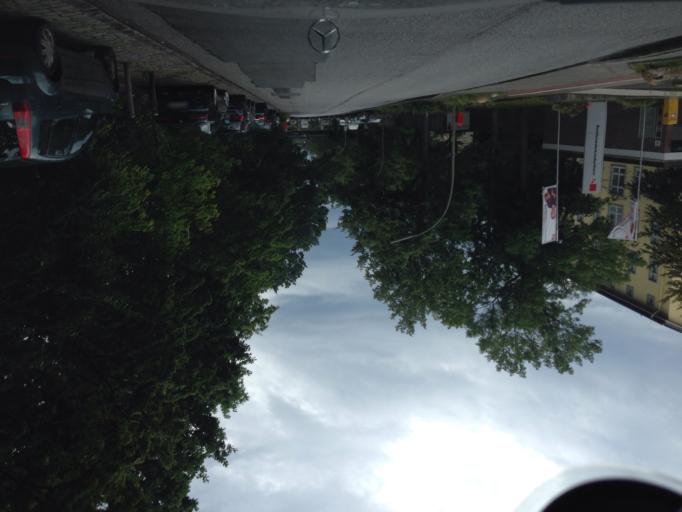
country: DE
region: Hamburg
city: Steilshoop
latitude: 53.5942
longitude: 10.0742
